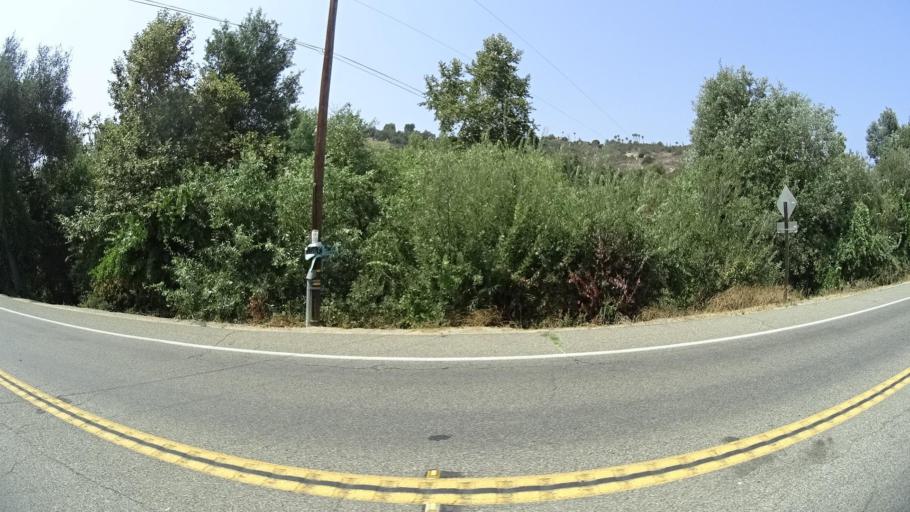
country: US
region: California
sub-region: San Diego County
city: Bonsall
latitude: 33.3094
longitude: -117.2284
